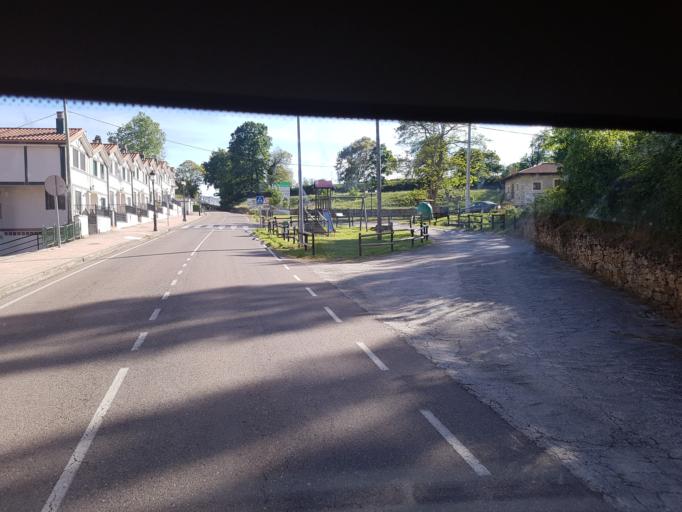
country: ES
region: Castille and Leon
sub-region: Provincia de Burgos
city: Espinosa de los Monteros
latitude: 43.0753
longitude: -3.5566
